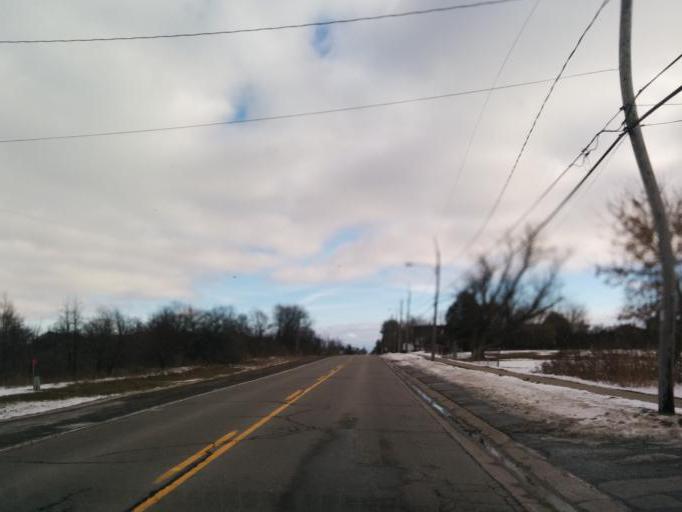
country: CA
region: Ontario
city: Brantford
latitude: 42.9667
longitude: -80.0645
